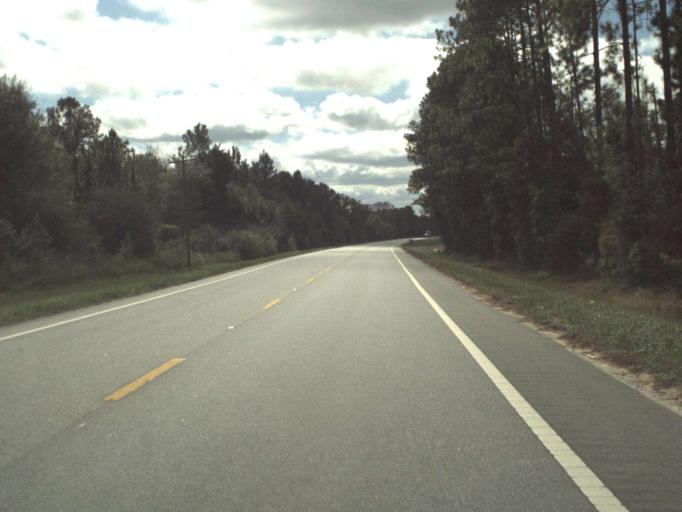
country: US
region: Florida
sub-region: Calhoun County
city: Blountstown
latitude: 30.3363
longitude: -85.2196
